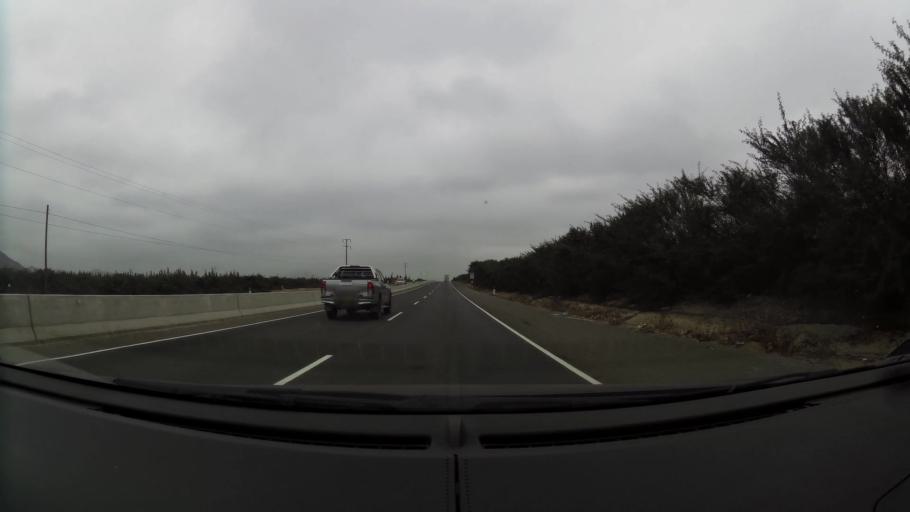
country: PE
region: La Libertad
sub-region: Viru
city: Chao
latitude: -8.4806
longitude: -78.7017
